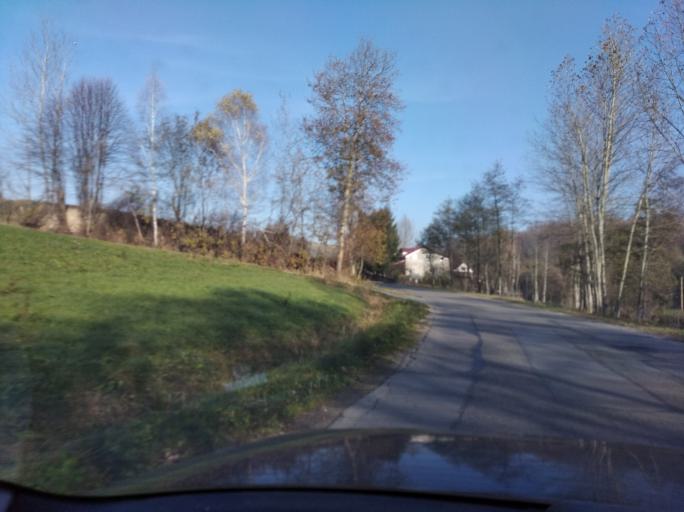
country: PL
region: Subcarpathian Voivodeship
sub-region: Powiat ropczycko-sedziszowski
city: Wielopole Skrzynskie
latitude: 49.9400
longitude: 21.5784
